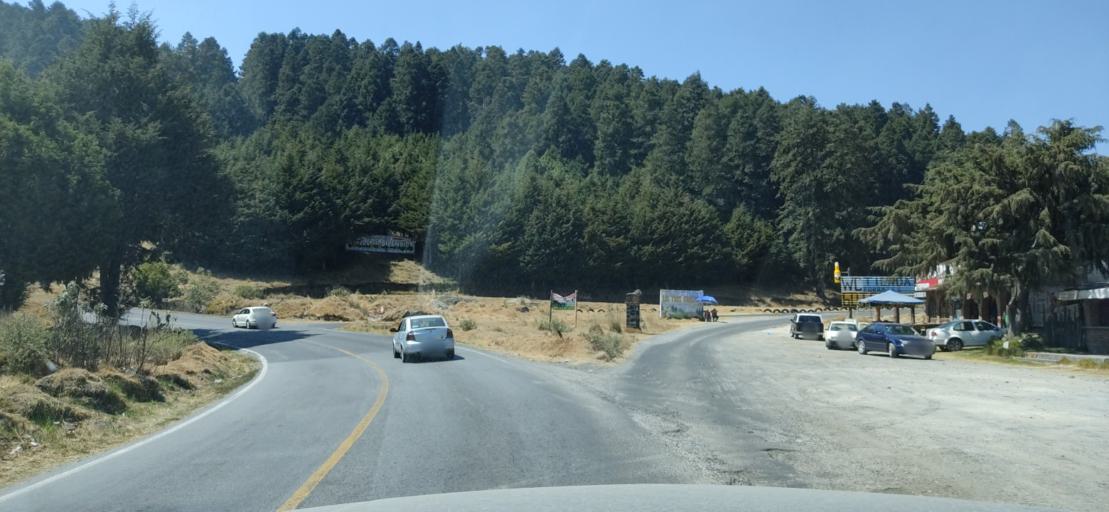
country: MX
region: Mexico
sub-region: Ocoyoacac
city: San Jeronimo Acazulco
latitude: 19.2807
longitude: -99.3806
